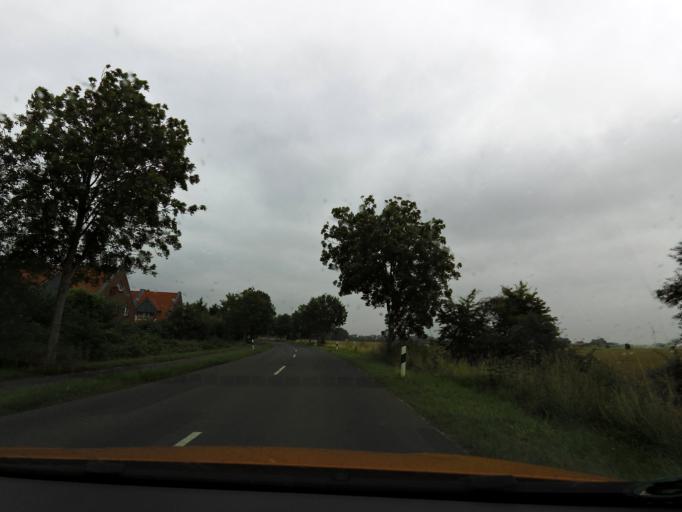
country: DE
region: Lower Saxony
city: Wirdum
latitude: 53.4985
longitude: 7.1061
